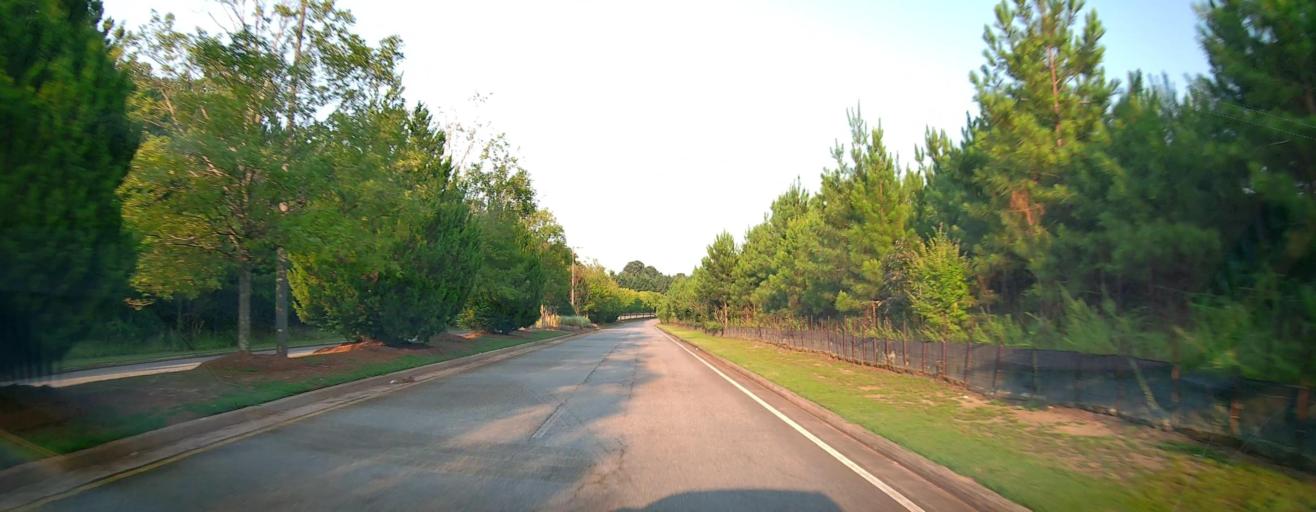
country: US
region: Georgia
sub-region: Bibb County
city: Macon
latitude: 32.9376
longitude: -83.7363
